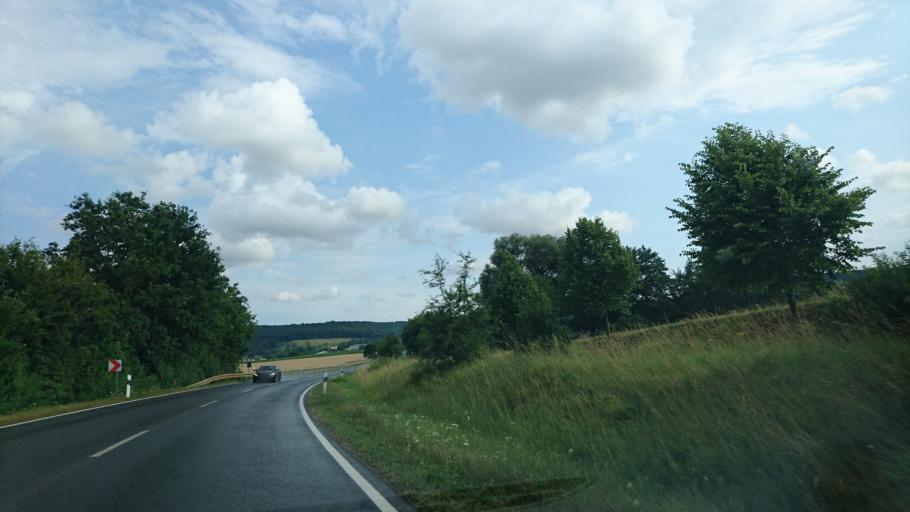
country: DE
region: Bavaria
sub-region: Regierungsbezirk Mittelfranken
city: Thalmassing
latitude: 49.0987
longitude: 11.2090
